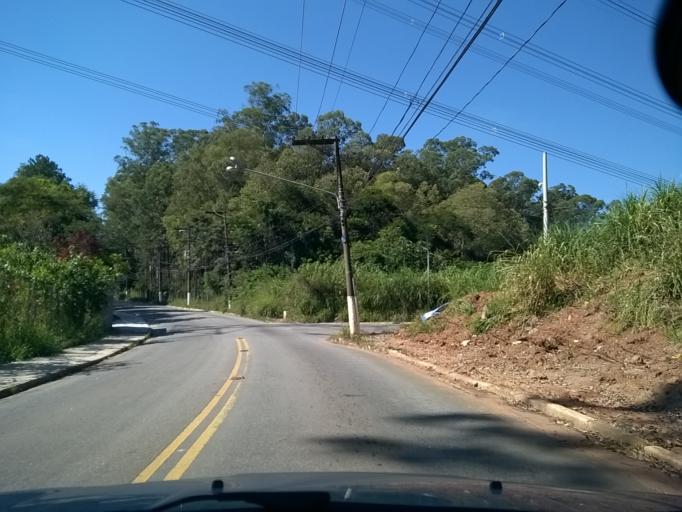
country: BR
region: Sao Paulo
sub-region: Caieiras
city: Caieiras
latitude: -23.3988
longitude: -46.7433
